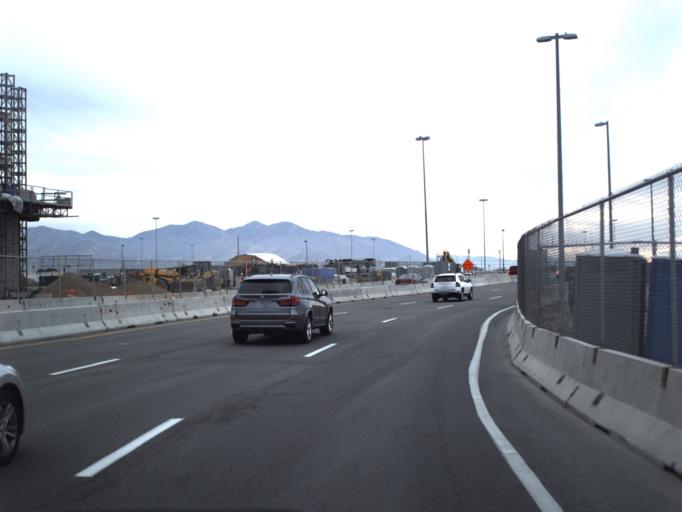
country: US
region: Utah
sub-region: Salt Lake County
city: West Valley City
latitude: 40.7817
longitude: -111.9865
